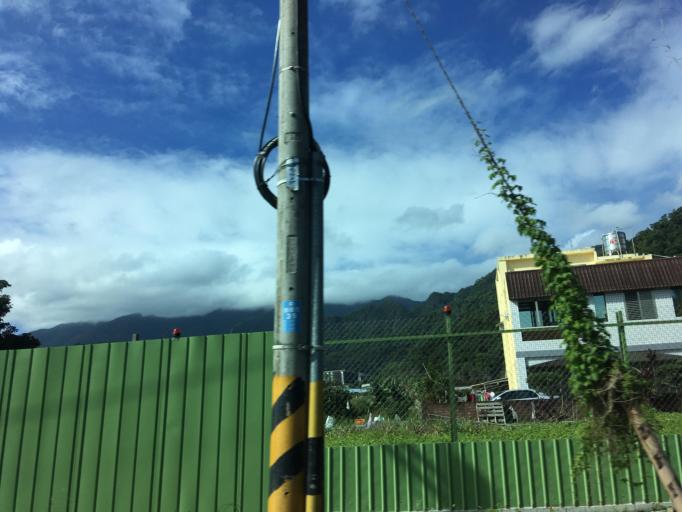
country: TW
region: Taiwan
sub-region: Yilan
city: Yilan
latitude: 24.8245
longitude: 121.7620
